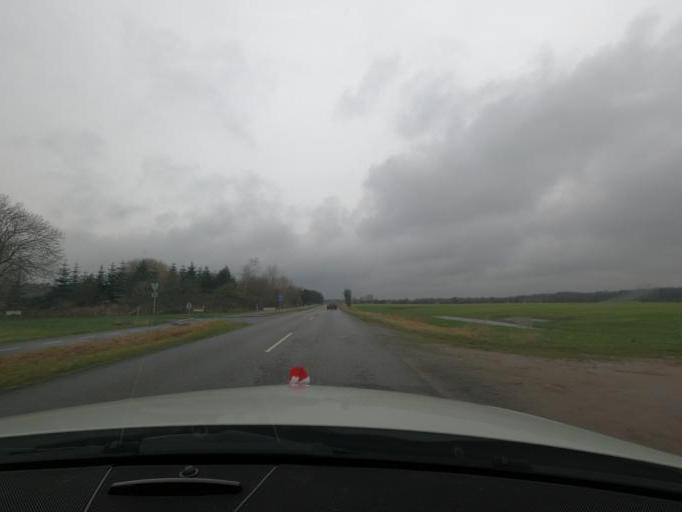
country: DK
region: South Denmark
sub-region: Haderslev Kommune
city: Starup
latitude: 55.2075
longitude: 9.5173
